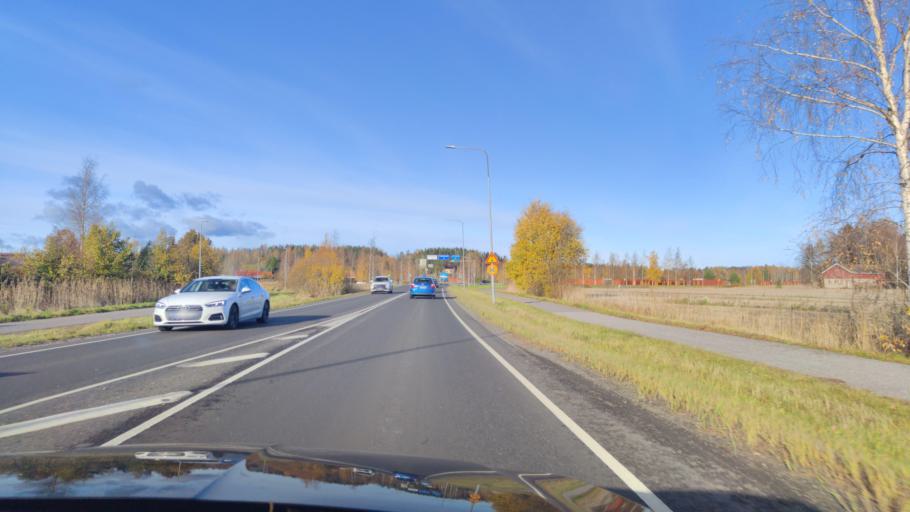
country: FI
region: Varsinais-Suomi
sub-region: Turku
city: Kaarina
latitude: 60.4343
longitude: 22.3844
